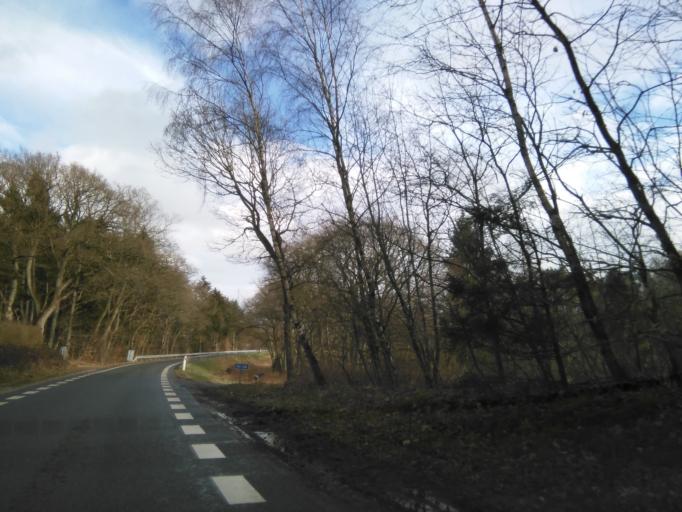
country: DK
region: Central Jutland
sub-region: Skanderborg Kommune
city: Ry
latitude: 56.1092
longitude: 9.7959
